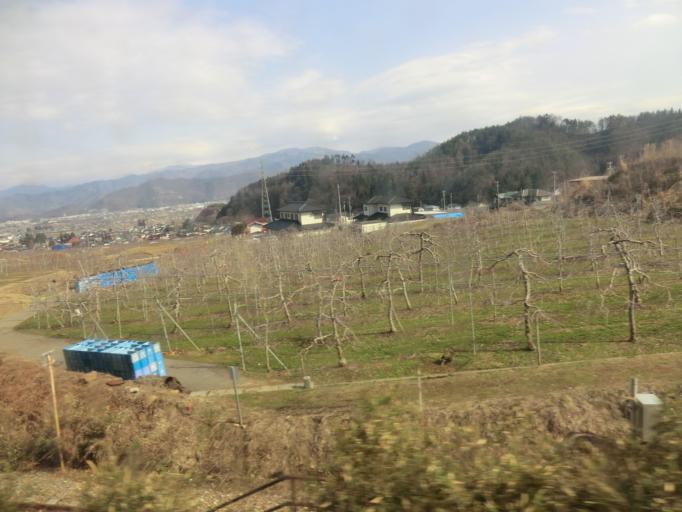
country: JP
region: Nagano
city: Nagano-shi
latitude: 36.5202
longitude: 138.0753
